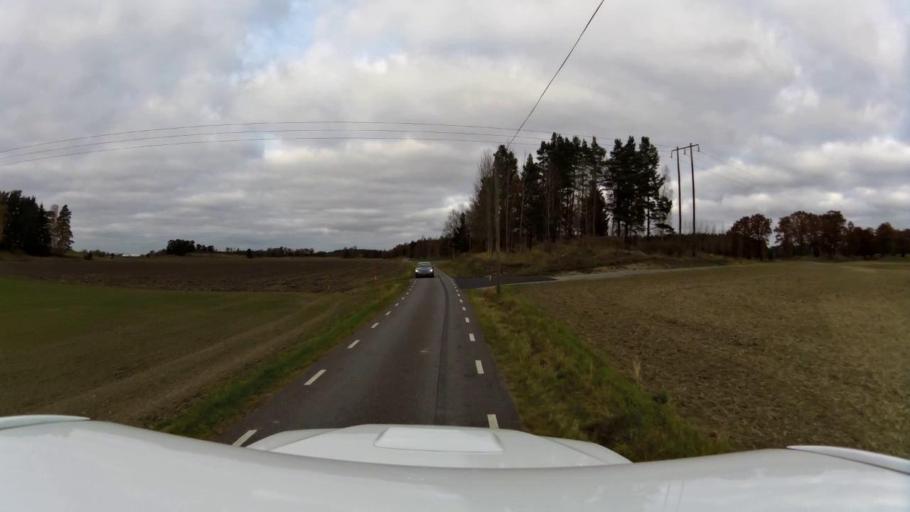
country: SE
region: OEstergoetland
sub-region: Linkopings Kommun
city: Linghem
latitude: 58.3842
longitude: 15.8178
